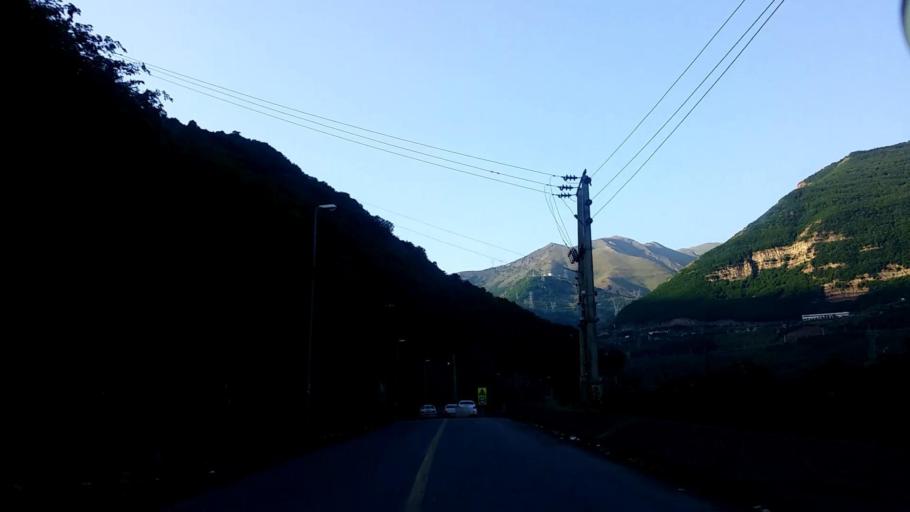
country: IR
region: Mazandaran
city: Chalus
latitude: 36.2438
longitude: 51.3013
